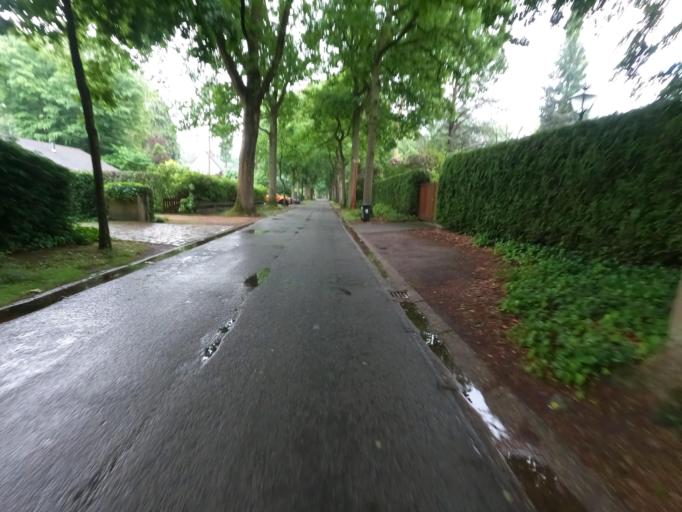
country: BE
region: Flanders
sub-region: Provincie Antwerpen
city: Kalmthout
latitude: 51.3662
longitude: 4.4752
